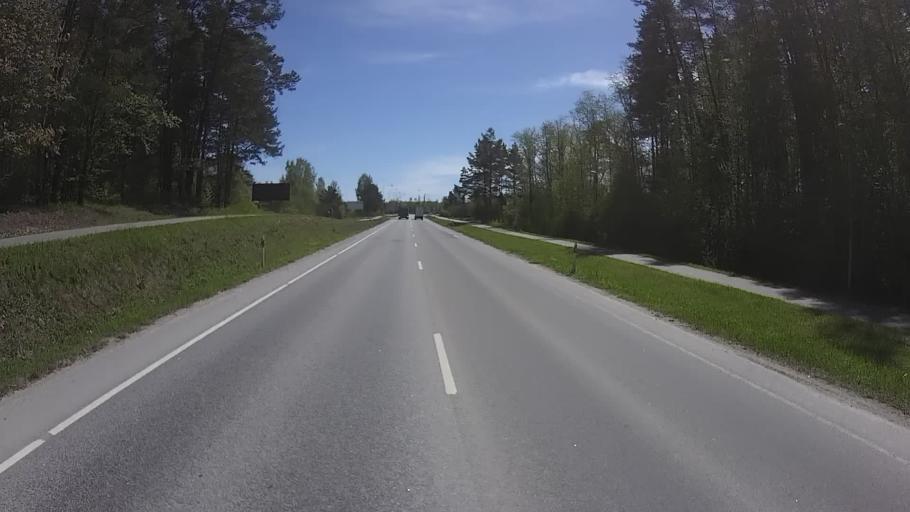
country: EE
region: Vorumaa
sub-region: Voru linn
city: Voru
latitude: 57.8182
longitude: 27.0258
